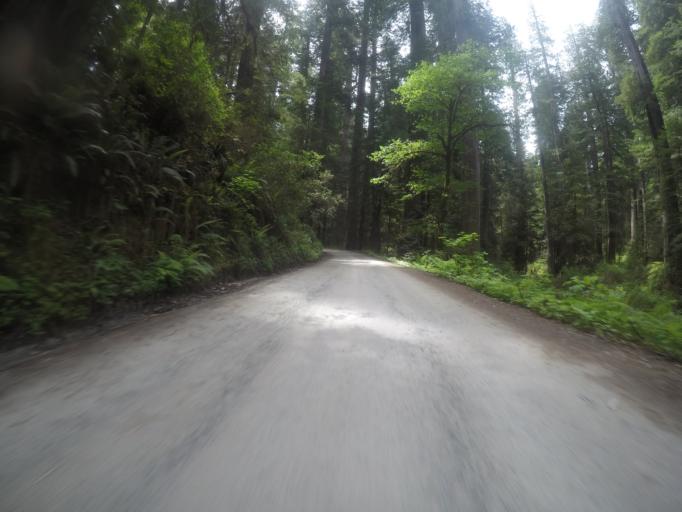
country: US
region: California
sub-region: Del Norte County
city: Bertsch-Oceanview
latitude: 41.7649
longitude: -124.1296
